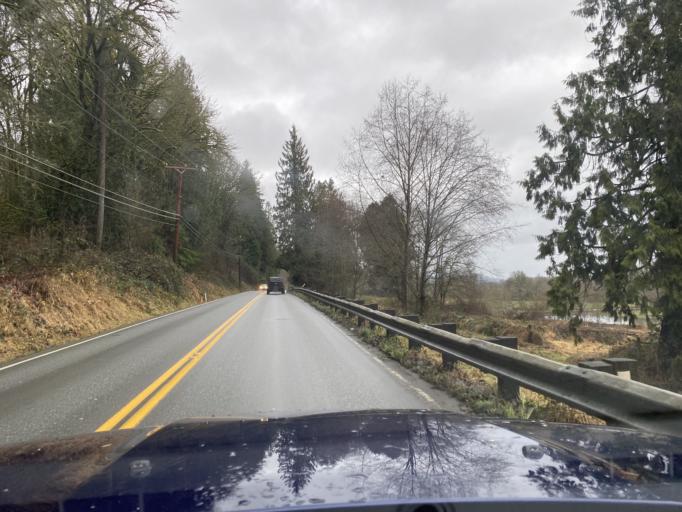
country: US
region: Washington
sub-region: King County
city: Union Hill-Novelty Hill
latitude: 47.7064
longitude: -122.0045
